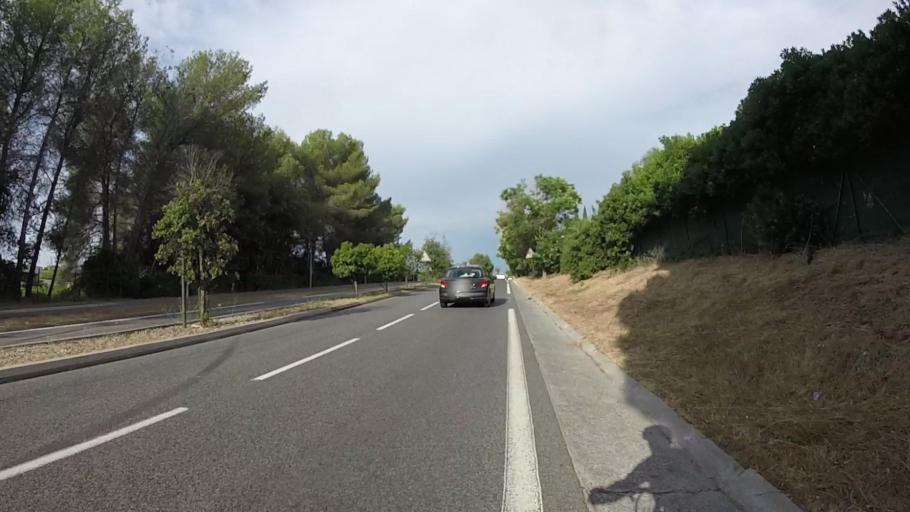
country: FR
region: Provence-Alpes-Cote d'Azur
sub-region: Departement des Alpes-Maritimes
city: Biot
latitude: 43.6159
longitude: 7.0826
